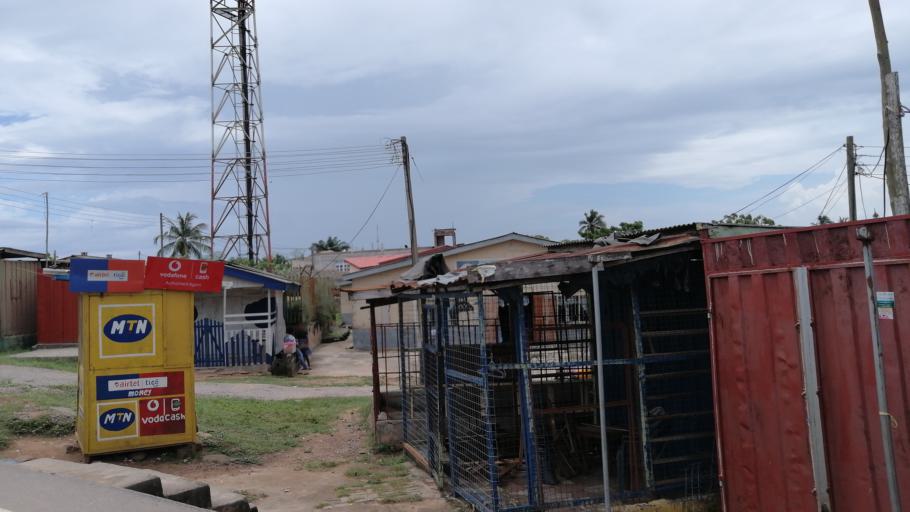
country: GH
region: Central
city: Elmina
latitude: 5.0924
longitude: -1.3459
